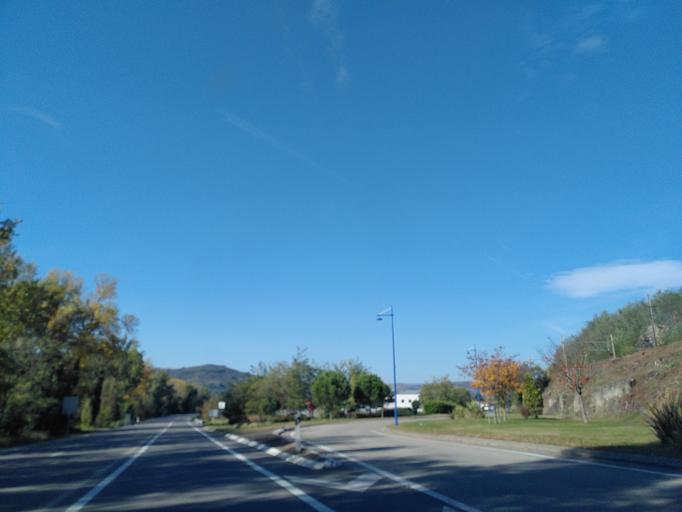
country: FR
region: Rhone-Alpes
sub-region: Departement de la Drome
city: Saint-Vallier
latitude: 45.1643
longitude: 4.8237
